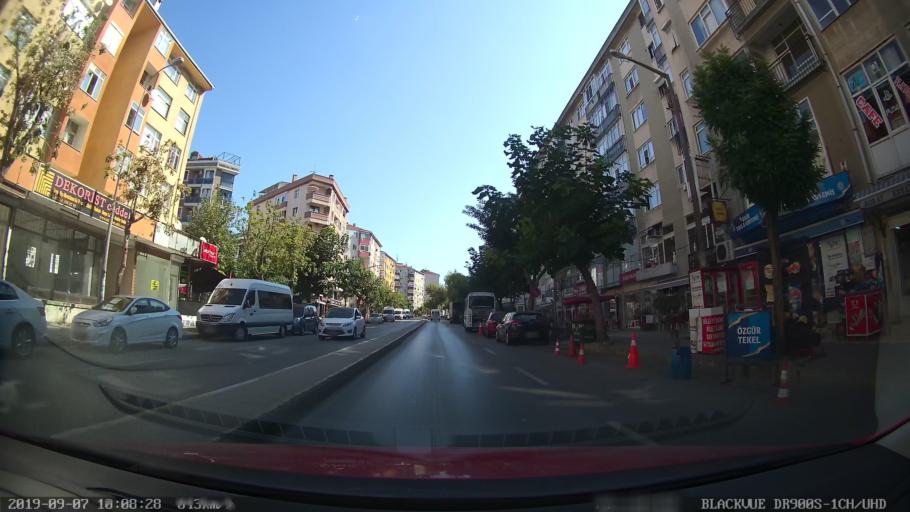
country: TR
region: Istanbul
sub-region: Atasehir
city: Atasehir
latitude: 40.9487
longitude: 29.1150
